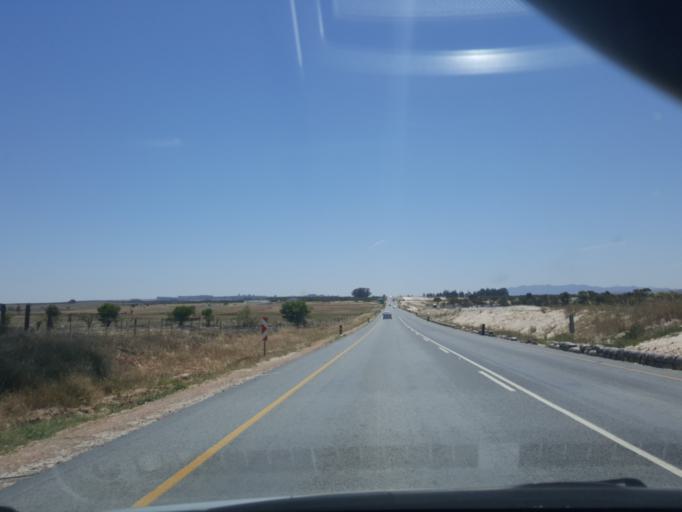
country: ZA
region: Western Cape
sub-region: City of Cape Town
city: Atlantis
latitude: -33.5761
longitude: 18.6160
